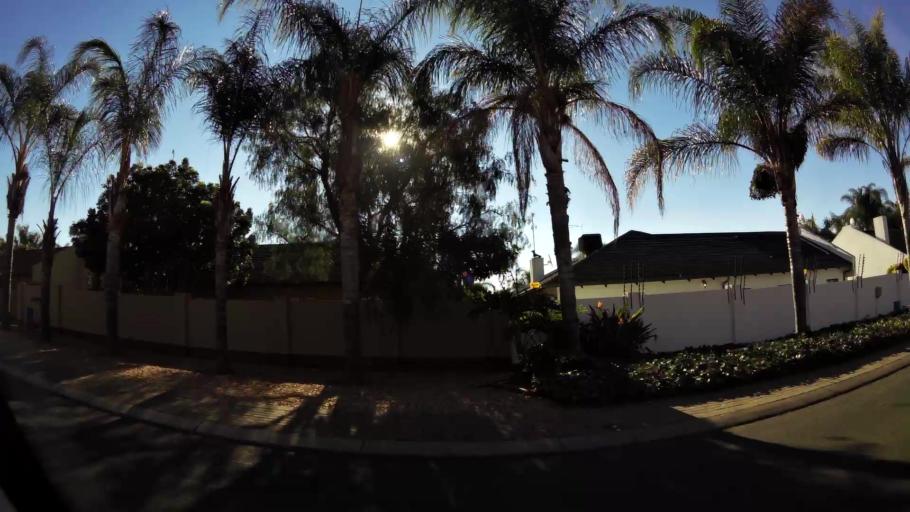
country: ZA
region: Limpopo
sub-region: Capricorn District Municipality
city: Polokwane
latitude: -23.8869
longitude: 29.4926
